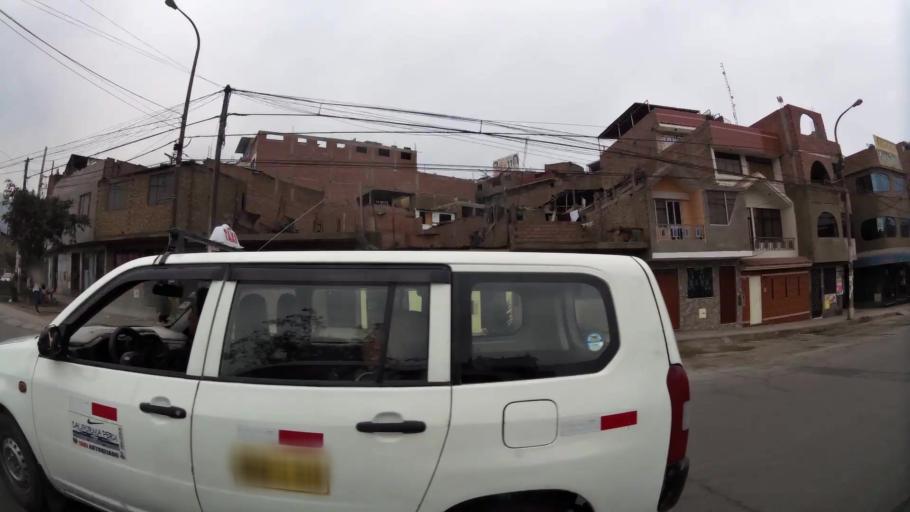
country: PE
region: Lima
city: Lima
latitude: -12.0097
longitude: -76.9968
